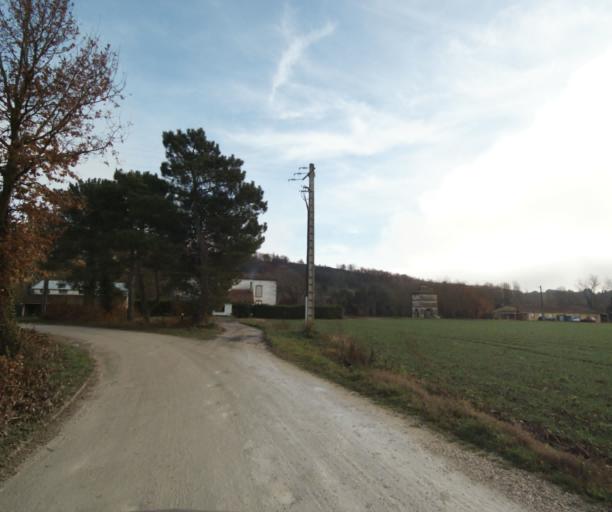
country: FR
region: Midi-Pyrenees
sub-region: Departement de la Haute-Garonne
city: Villemur-sur-Tarn
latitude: 43.8759
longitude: 1.4954
